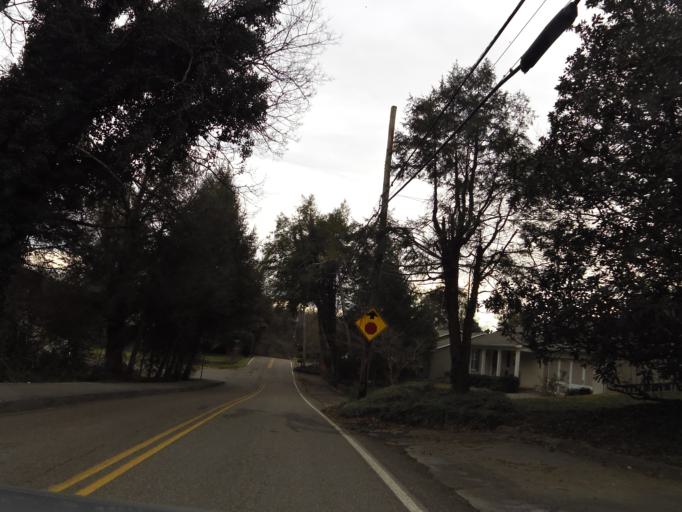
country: US
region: Tennessee
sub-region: Knox County
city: Knoxville
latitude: 35.9325
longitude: -83.9676
